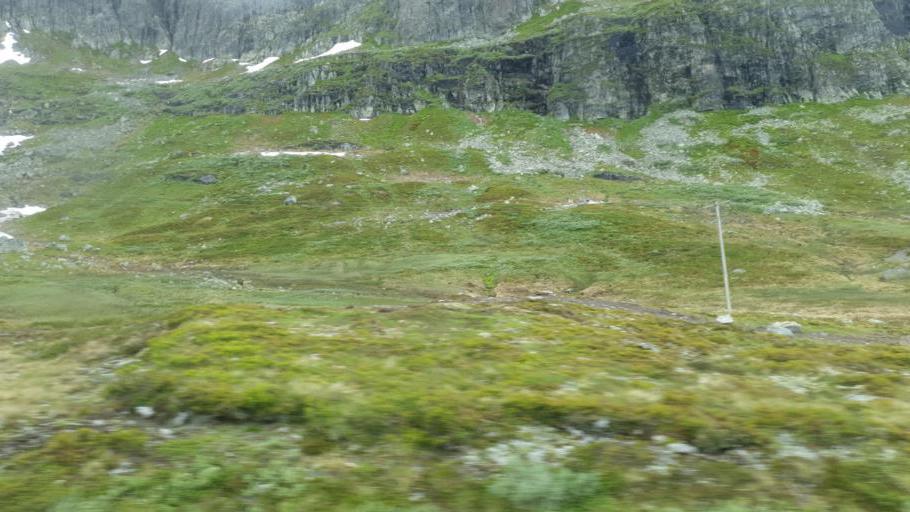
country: NO
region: Oppland
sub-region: Vestre Slidre
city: Slidre
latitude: 61.3019
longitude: 8.8079
